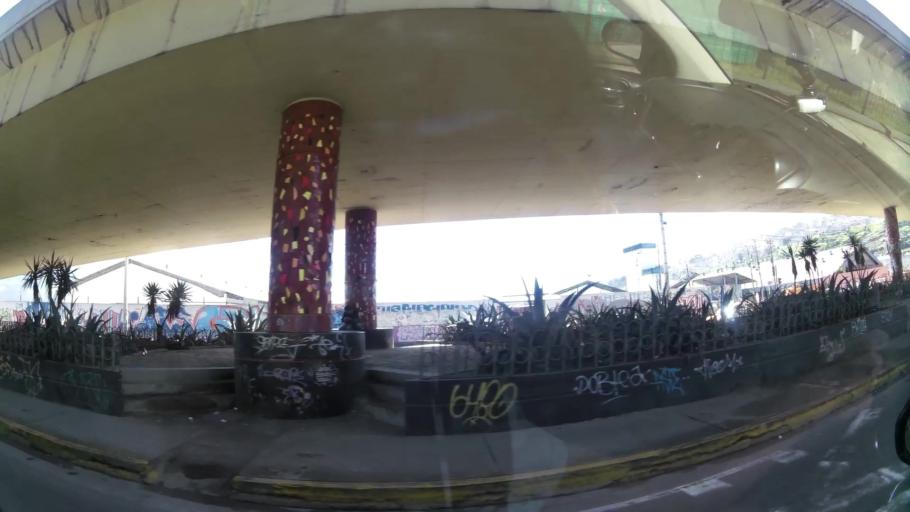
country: EC
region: Pichincha
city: Quito
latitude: -0.2892
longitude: -78.5393
